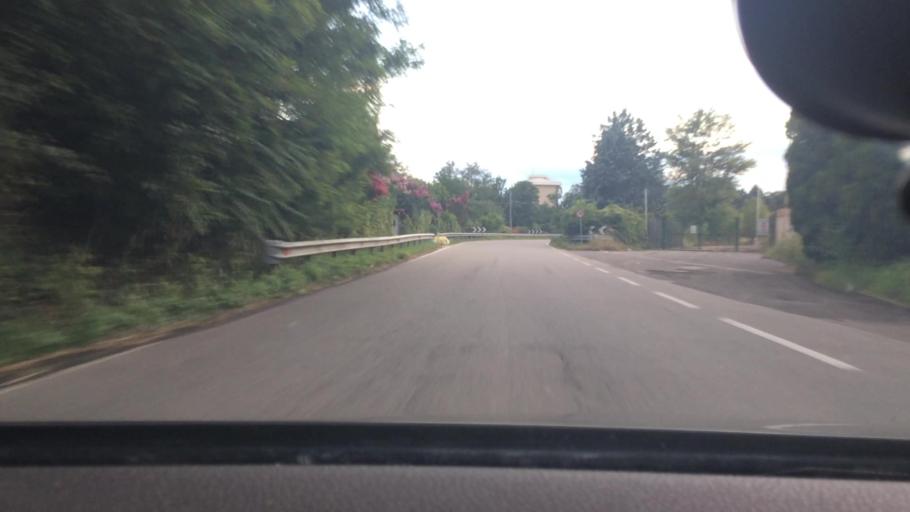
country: IT
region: Lombardy
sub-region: Citta metropolitana di Milano
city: Pregnana Milanese
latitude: 45.5187
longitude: 9.0144
